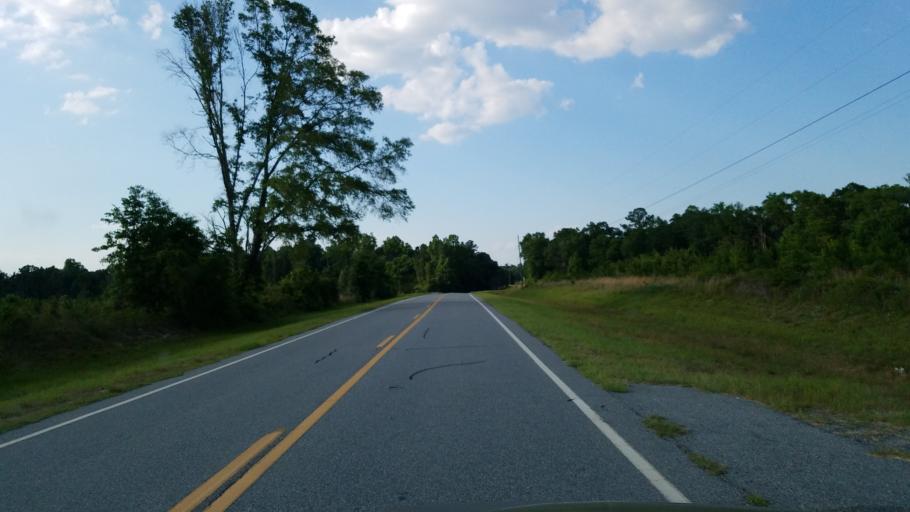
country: US
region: Georgia
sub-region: Echols County
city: Statenville
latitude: 30.7832
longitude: -83.0553
